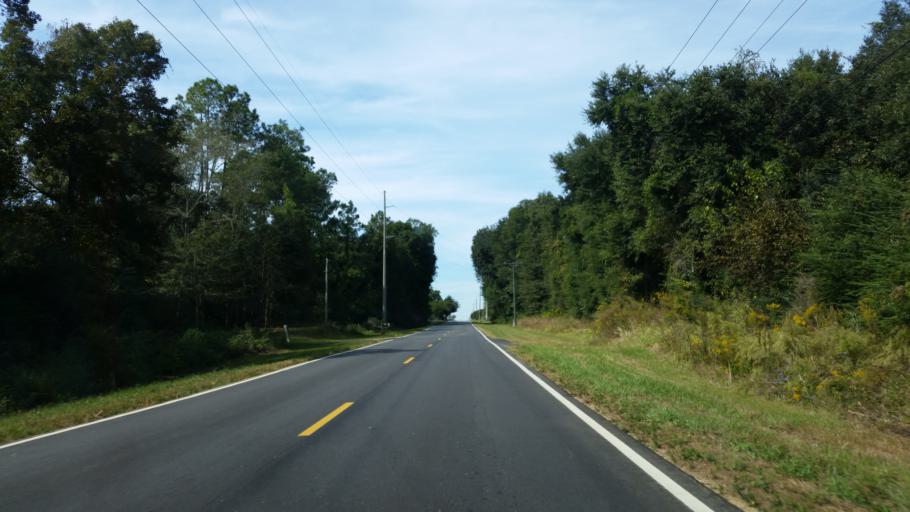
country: US
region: Alabama
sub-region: Baldwin County
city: Loxley
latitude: 30.6331
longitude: -87.7038
